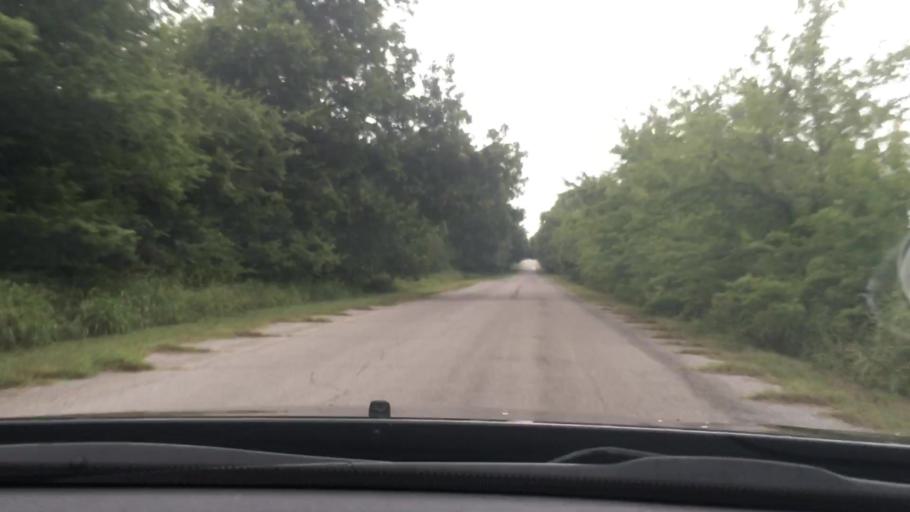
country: US
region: Oklahoma
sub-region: Murray County
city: Davis
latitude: 34.4593
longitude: -97.1426
